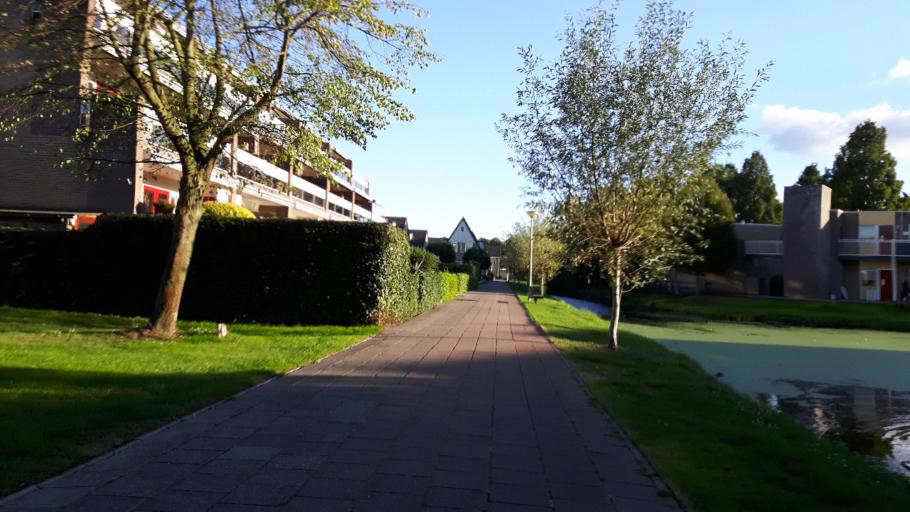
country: NL
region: Utrecht
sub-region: Gemeente Oudewater
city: Oudewater
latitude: 52.0285
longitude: 4.8708
